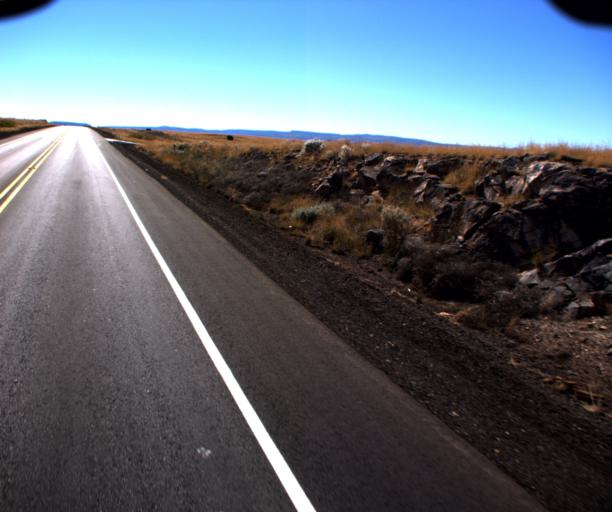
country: US
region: Arizona
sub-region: Apache County
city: Springerville
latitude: 34.2449
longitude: -109.3482
